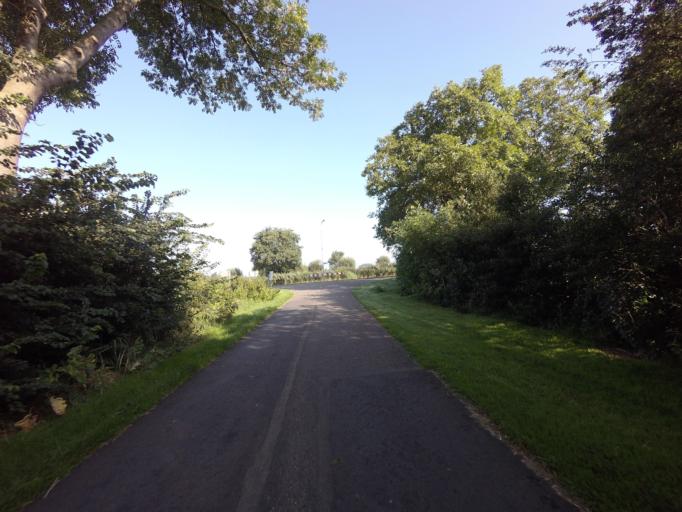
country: NL
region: Overijssel
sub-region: Gemeente Steenwijkerland
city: Blokzijl
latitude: 52.7489
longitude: 6.0000
